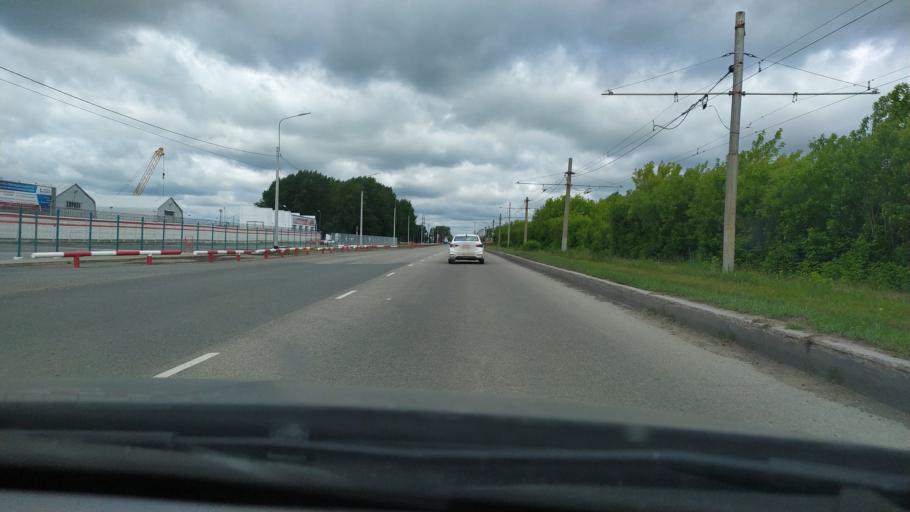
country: RU
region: Perm
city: Kondratovo
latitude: 57.9276
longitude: 56.1334
